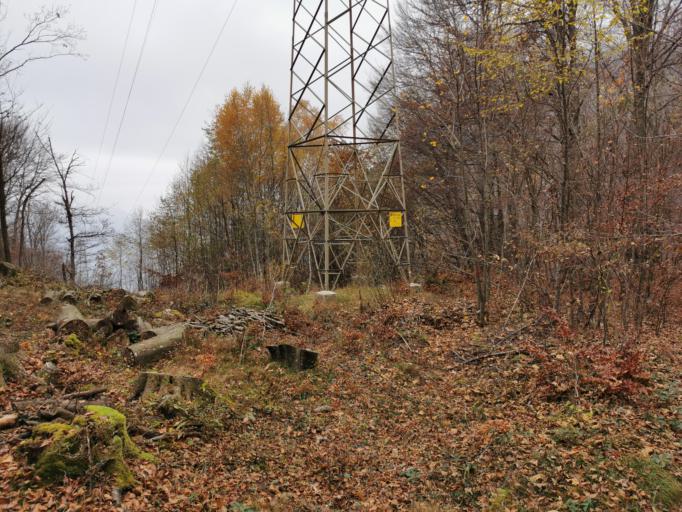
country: IT
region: Lombardy
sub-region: Provincia di Lecco
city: Abbadia Lariana
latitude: 45.9064
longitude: 9.3722
